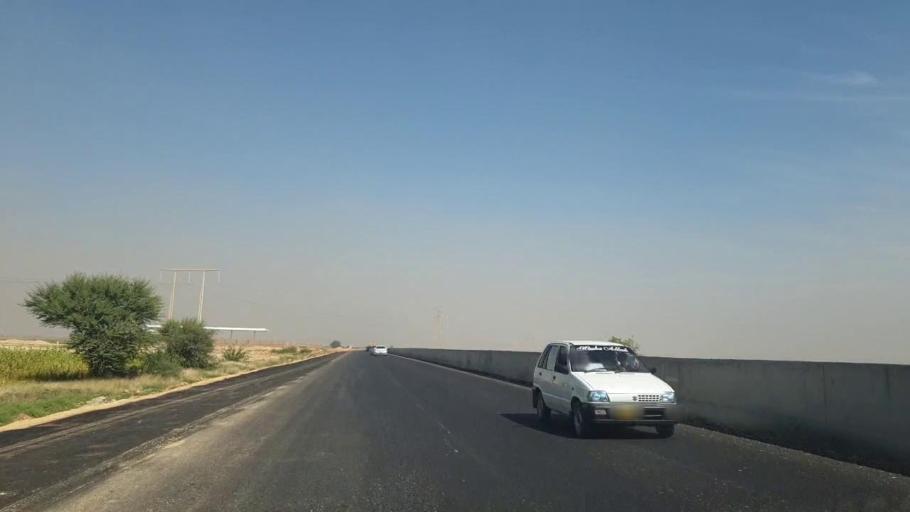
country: PK
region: Sindh
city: Jamshoro
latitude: 25.5332
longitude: 68.2829
